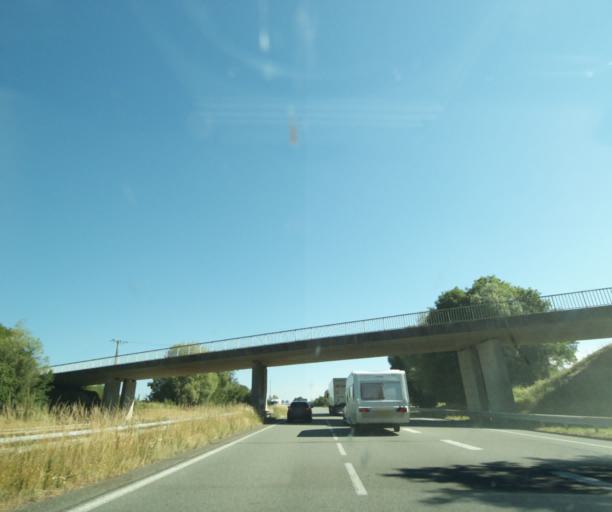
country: FR
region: Champagne-Ardenne
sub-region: Departement de la Haute-Marne
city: Avrecourt
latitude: 47.9921
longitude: 5.5121
